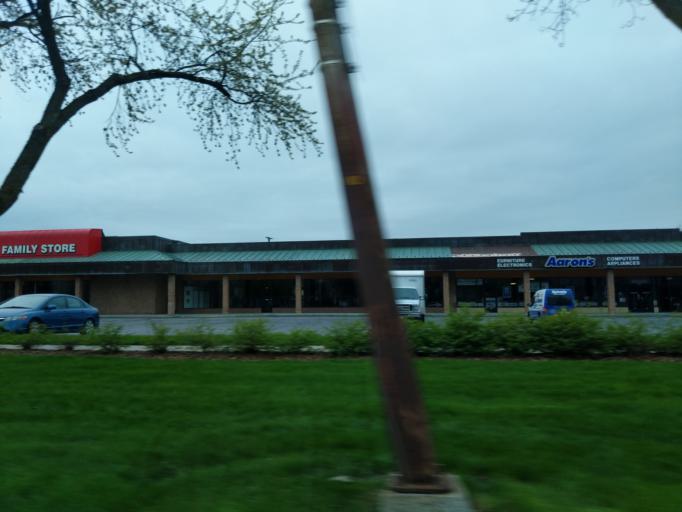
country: US
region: Michigan
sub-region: Midland County
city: Midland
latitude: 43.6201
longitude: -84.2201
